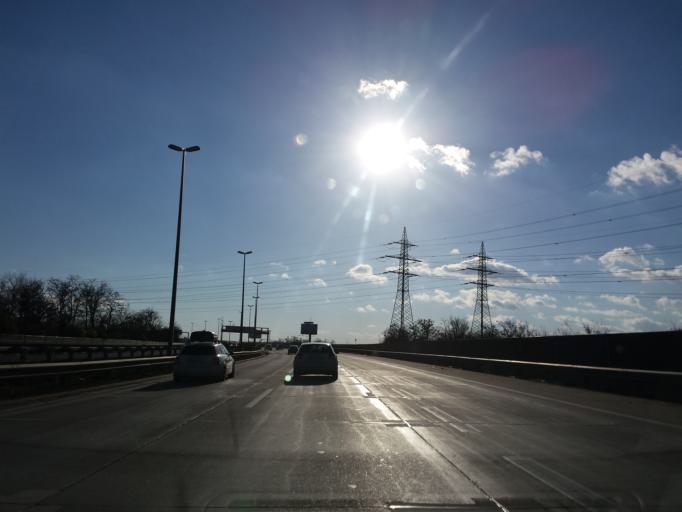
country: AT
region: Lower Austria
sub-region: Politischer Bezirk Wien-Umgebung
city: Schwechat
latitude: 48.1727
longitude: 16.4551
